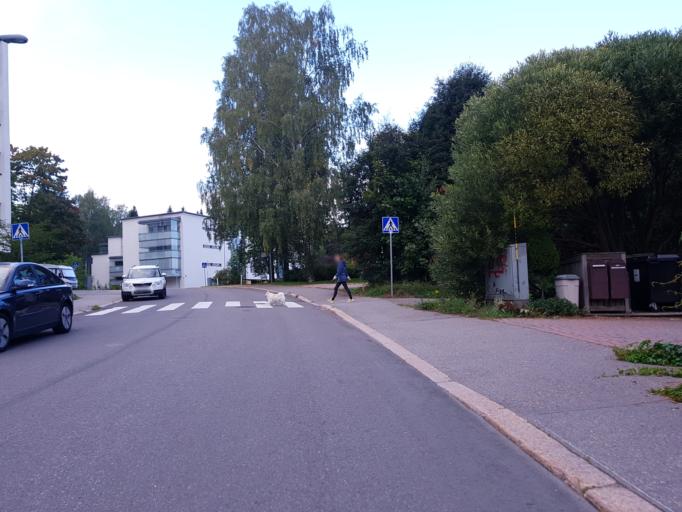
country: FI
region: Uusimaa
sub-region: Helsinki
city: Helsinki
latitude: 60.2336
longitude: 24.9383
